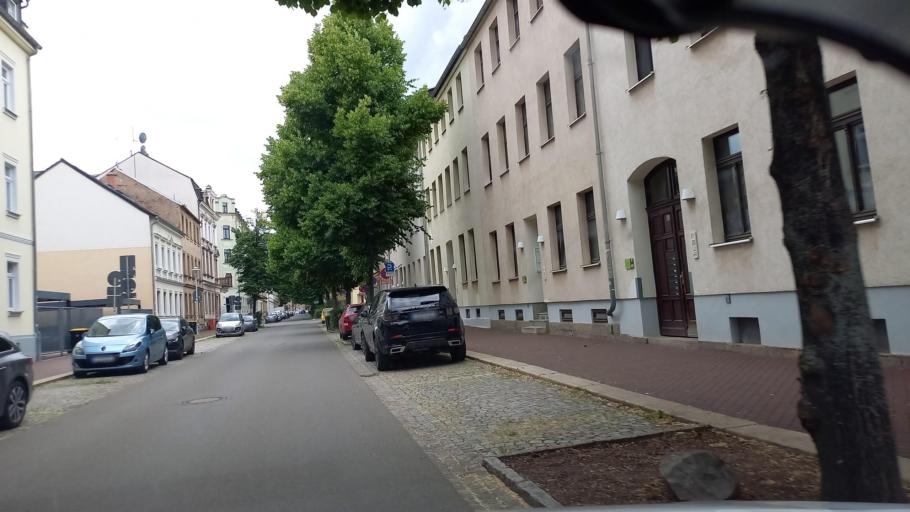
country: DE
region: Saxony
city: Zwickau
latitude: 50.7252
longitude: 12.4955
